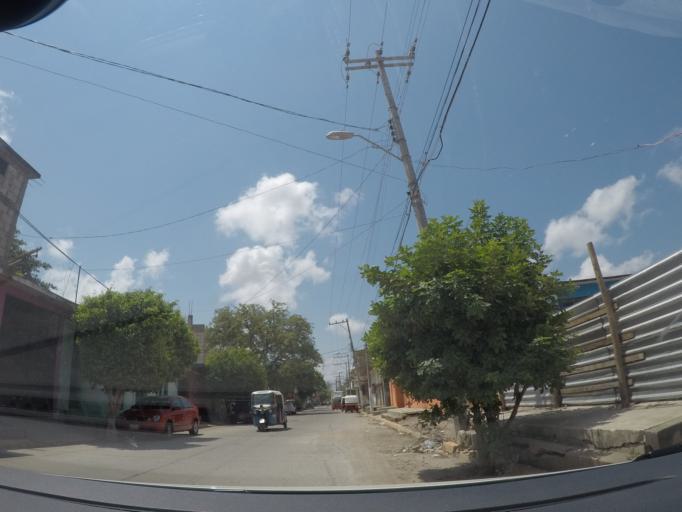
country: MX
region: Oaxaca
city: Juchitan de Zaragoza
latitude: 16.4373
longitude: -95.0178
